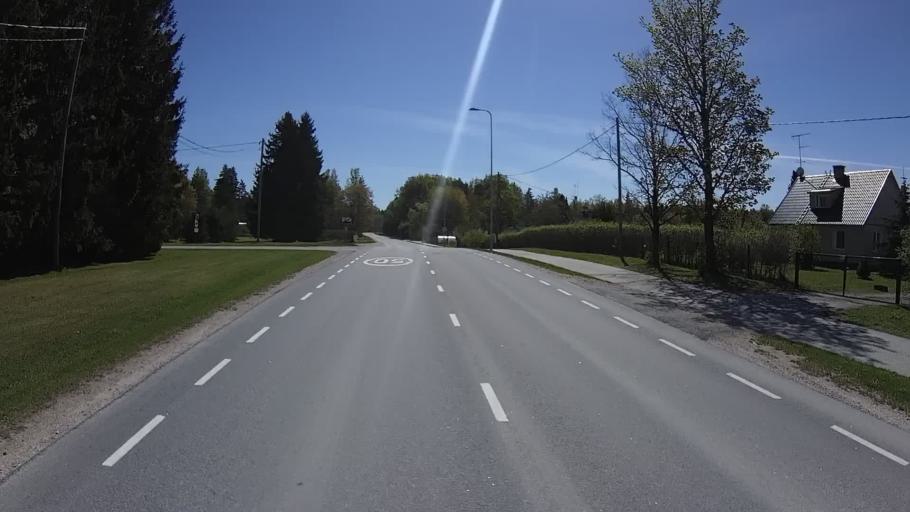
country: EE
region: Harju
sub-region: Raasiku vald
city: Raasiku
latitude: 59.1775
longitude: 25.1694
